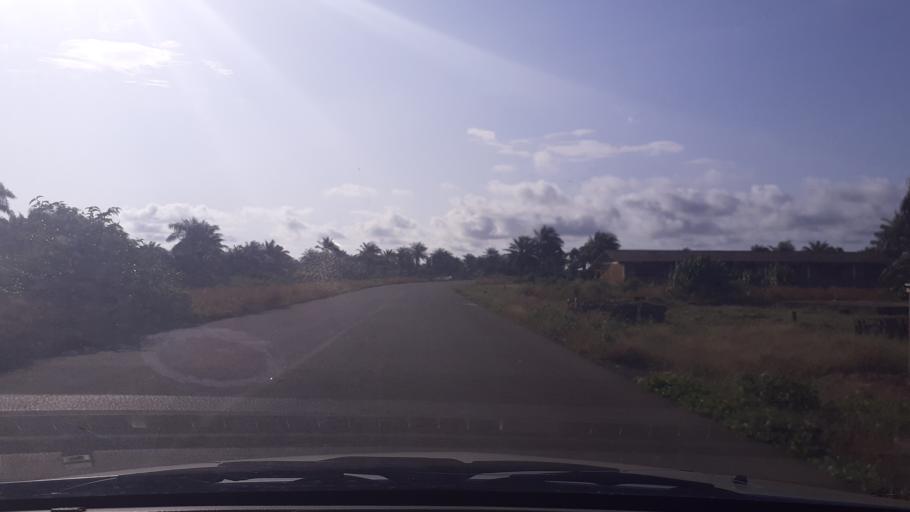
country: LR
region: Montserrado
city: Bensonville City
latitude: 6.1694
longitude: -10.4489
